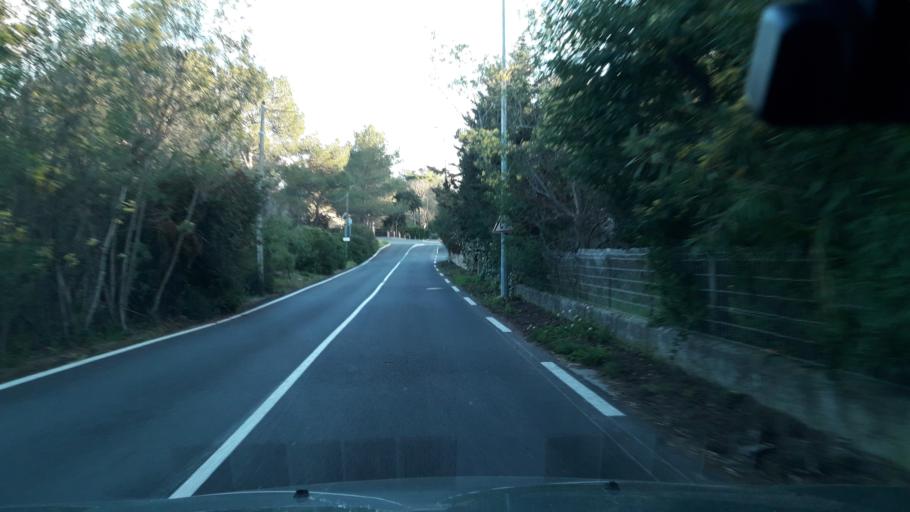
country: FR
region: Provence-Alpes-Cote d'Azur
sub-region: Departement du Var
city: Saint-Raphael
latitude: 43.4634
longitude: 6.7687
